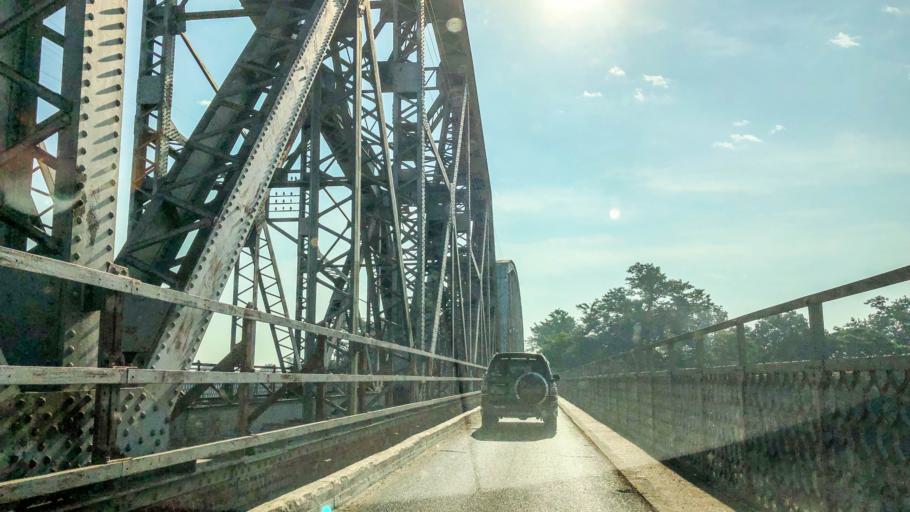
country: MM
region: Sagain
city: Sagaing
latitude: 21.8693
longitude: 95.9945
